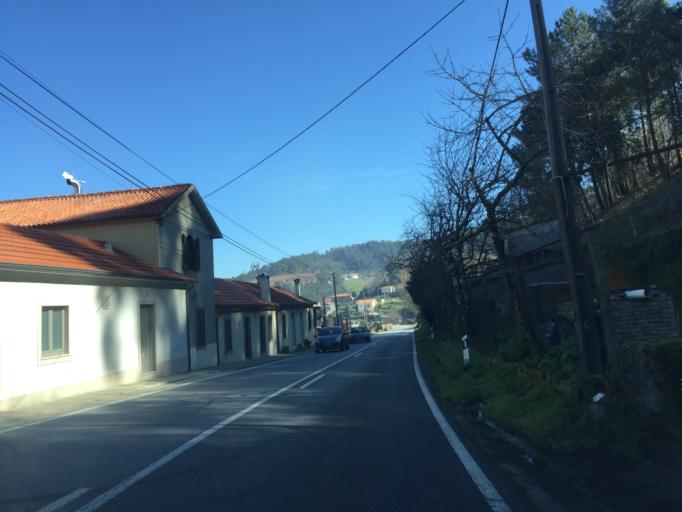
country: PT
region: Aveiro
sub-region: Vale de Cambra
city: Macieira de Cambra
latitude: 40.8933
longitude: -8.3350
